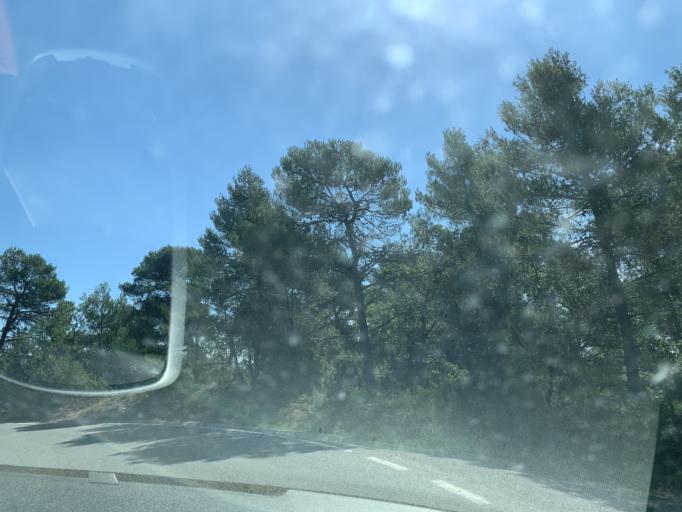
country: ES
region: Catalonia
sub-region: Provincia de Tarragona
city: Conesa
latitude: 41.5402
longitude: 1.3153
